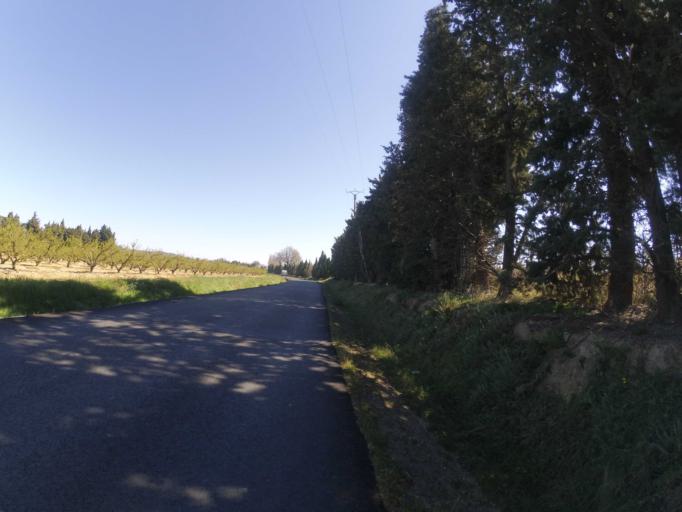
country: FR
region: Languedoc-Roussillon
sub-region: Departement des Pyrenees-Orientales
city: Millas
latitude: 42.6752
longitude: 2.6655
